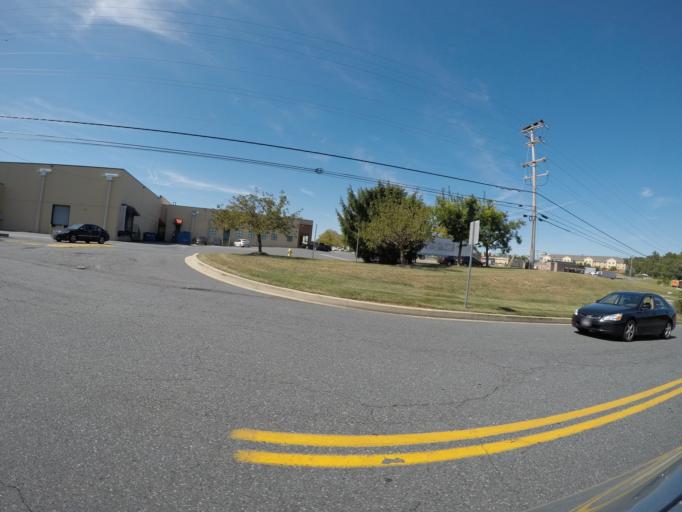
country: US
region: Maryland
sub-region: Harford County
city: Riverside
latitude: 39.4808
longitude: -76.2469
